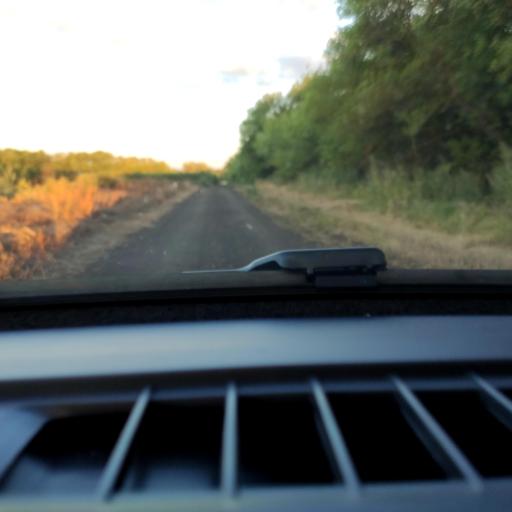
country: RU
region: Voronezj
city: Verkhnyaya Khava
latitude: 51.5943
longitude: 39.8423
